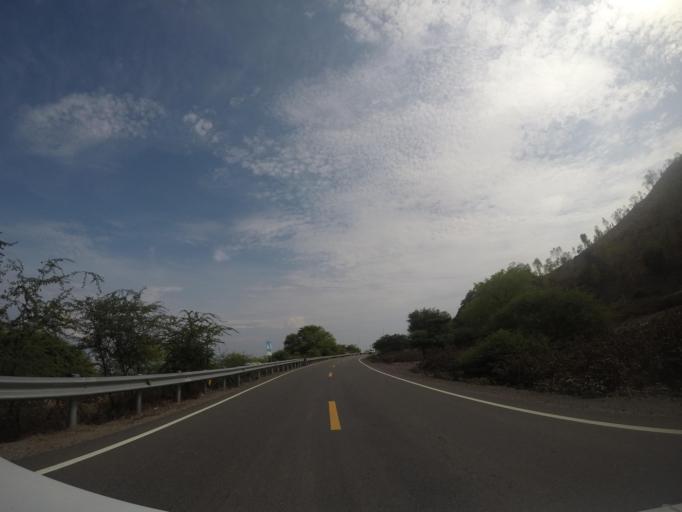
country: ID
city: Metinaro
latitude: -8.5275
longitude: 125.7097
